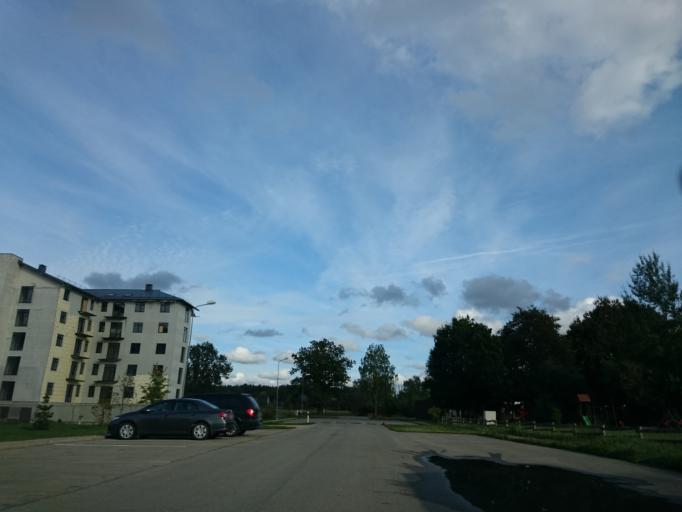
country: LV
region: Adazi
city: Adazi
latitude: 57.0704
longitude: 24.3548
